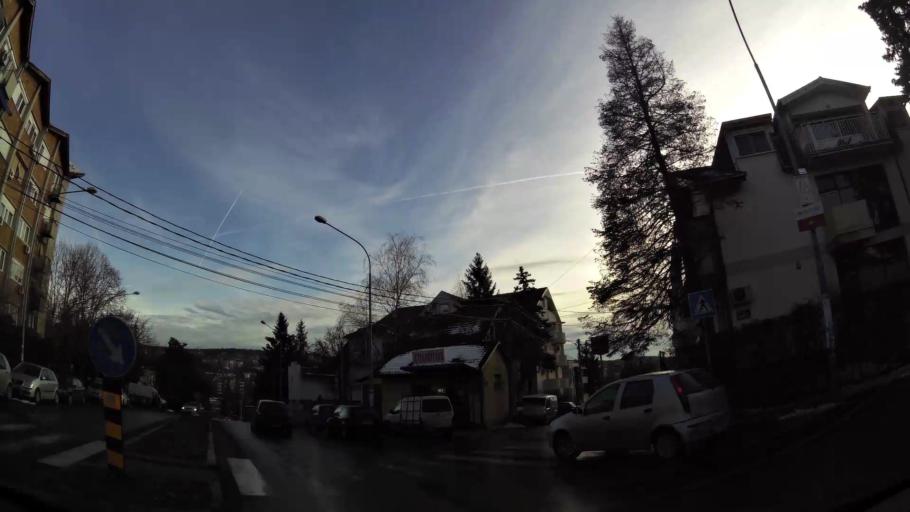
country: RS
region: Central Serbia
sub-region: Belgrade
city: Rakovica
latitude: 44.7526
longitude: 20.4506
